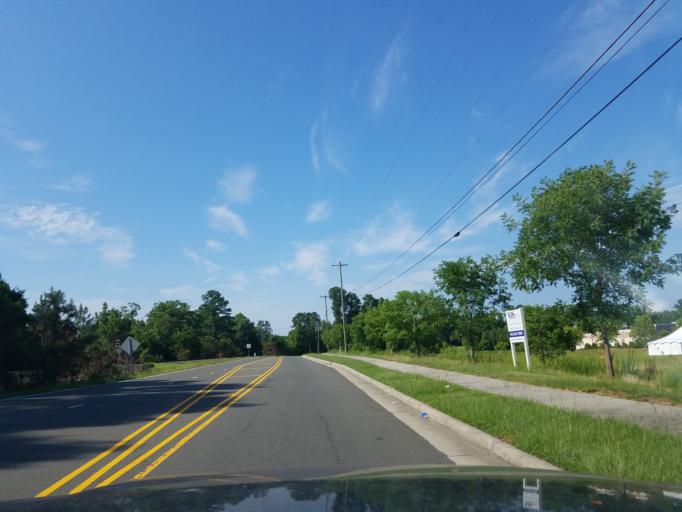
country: US
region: North Carolina
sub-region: Durham County
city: Gorman
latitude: 36.0287
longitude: -78.8398
